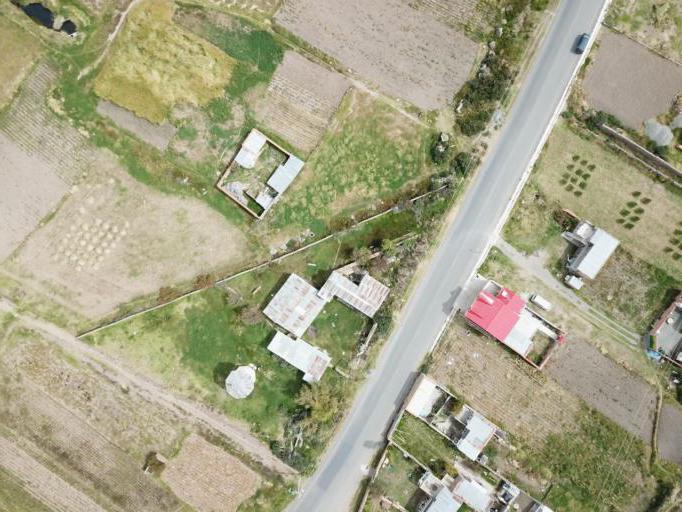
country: BO
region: La Paz
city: Achacachi
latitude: -16.0519
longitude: -68.8177
